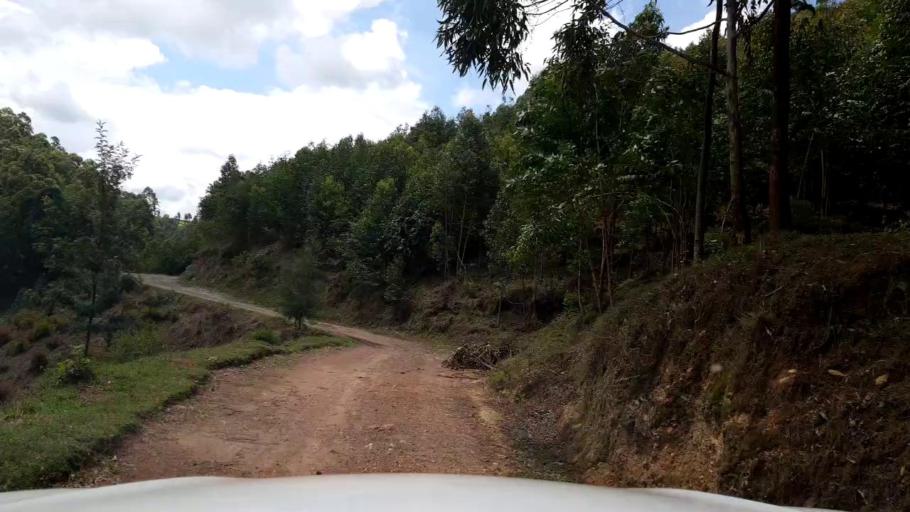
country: RW
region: Northern Province
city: Byumba
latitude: -1.5227
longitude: 30.1303
